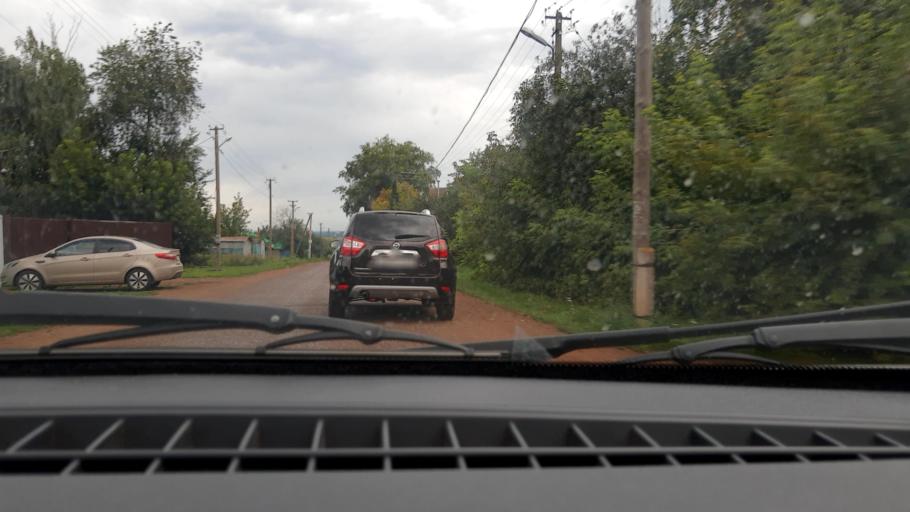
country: RU
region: Bashkortostan
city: Mikhaylovka
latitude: 54.8632
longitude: 55.8157
